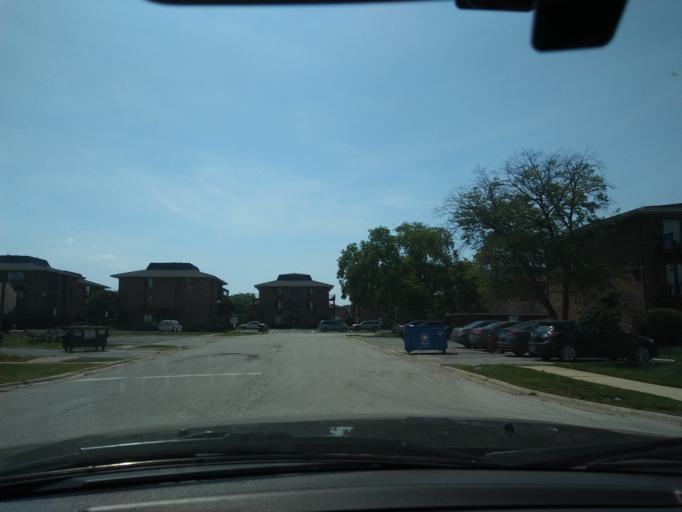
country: US
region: Illinois
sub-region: Cook County
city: Oak Forest
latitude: 41.6056
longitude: -87.7642
